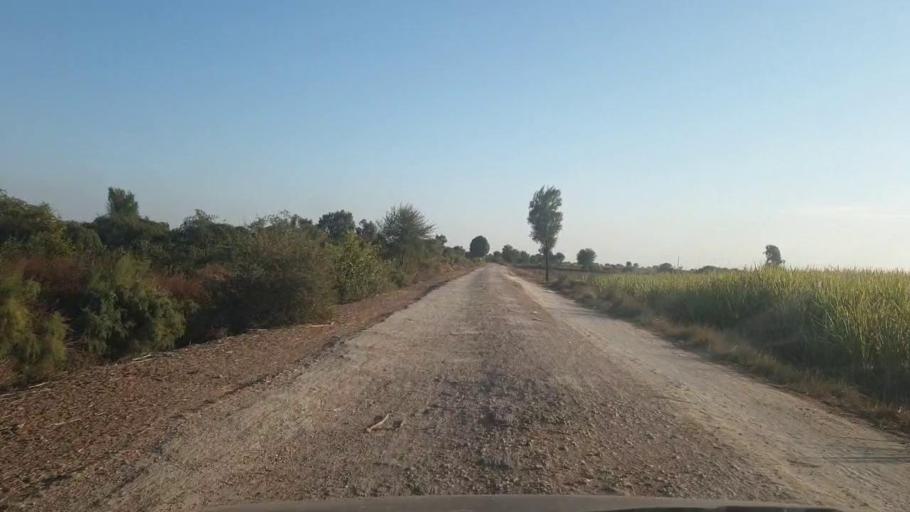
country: PK
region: Sindh
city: Sinjhoro
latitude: 26.0349
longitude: 68.8712
